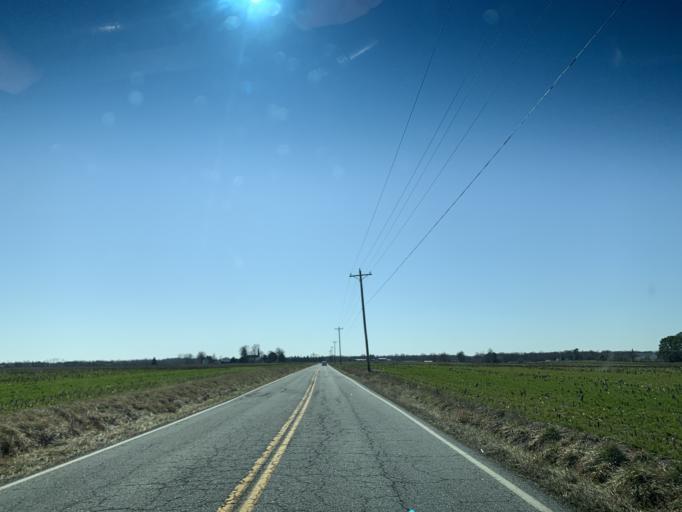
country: US
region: Maryland
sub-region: Cecil County
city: Charlestown
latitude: 39.4324
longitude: -75.9138
